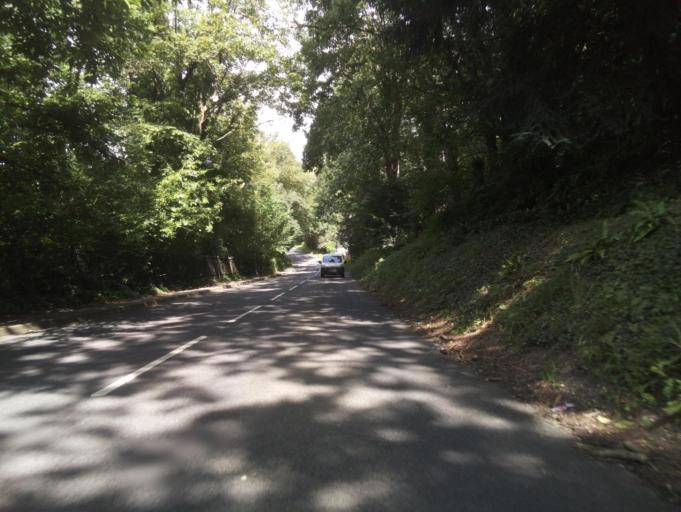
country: GB
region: England
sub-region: Dorset
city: Blandford Forum
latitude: 50.8666
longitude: -2.1712
